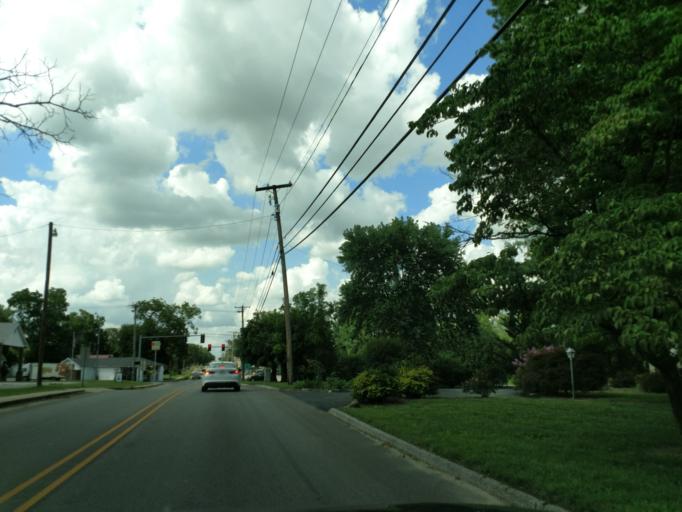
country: US
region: Arkansas
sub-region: Carroll County
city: Berryville
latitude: 36.3697
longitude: -93.5672
